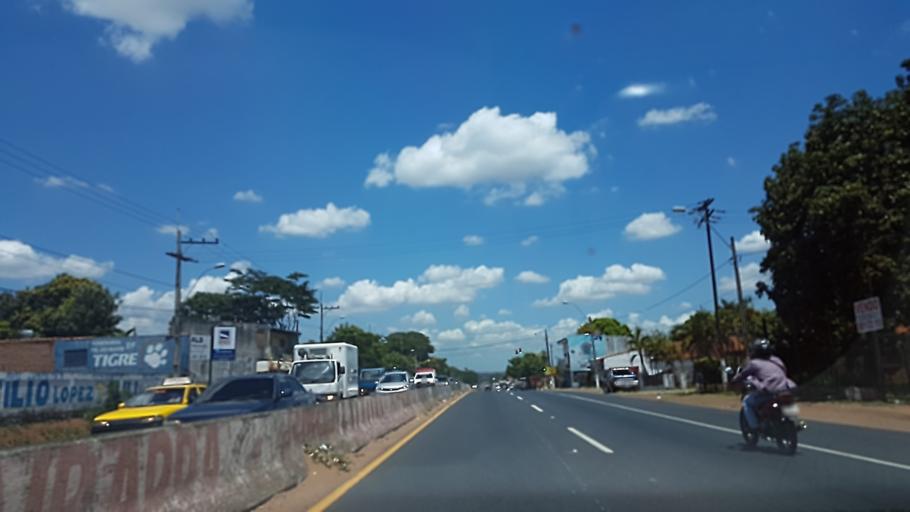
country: PY
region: Central
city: Capiata
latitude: -25.3495
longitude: -57.4531
